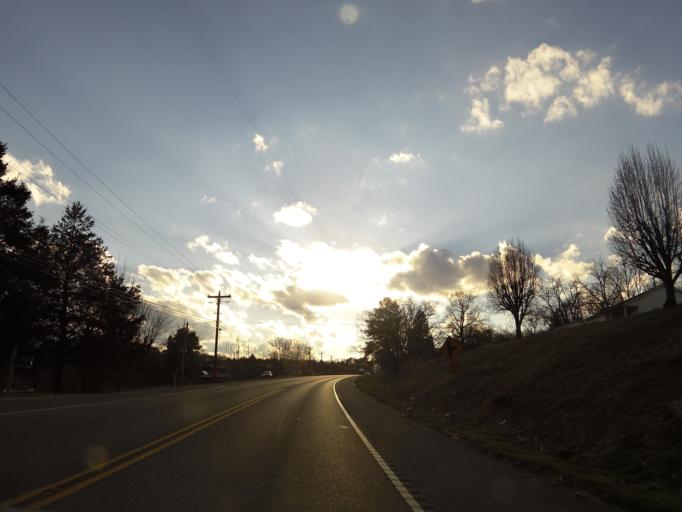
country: US
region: Tennessee
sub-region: Smith County
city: South Carthage
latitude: 36.2488
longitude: -86.0209
